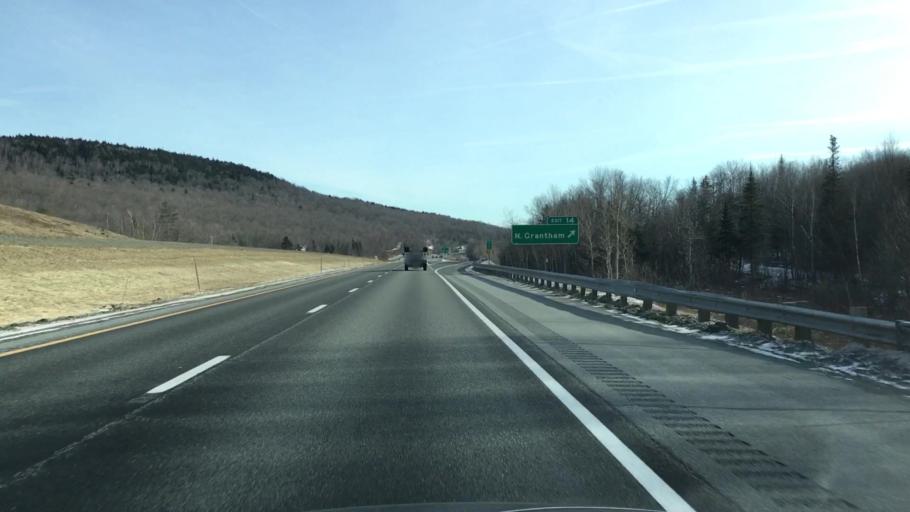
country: US
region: New Hampshire
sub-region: Grafton County
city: Enfield
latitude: 43.5697
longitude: -72.1537
